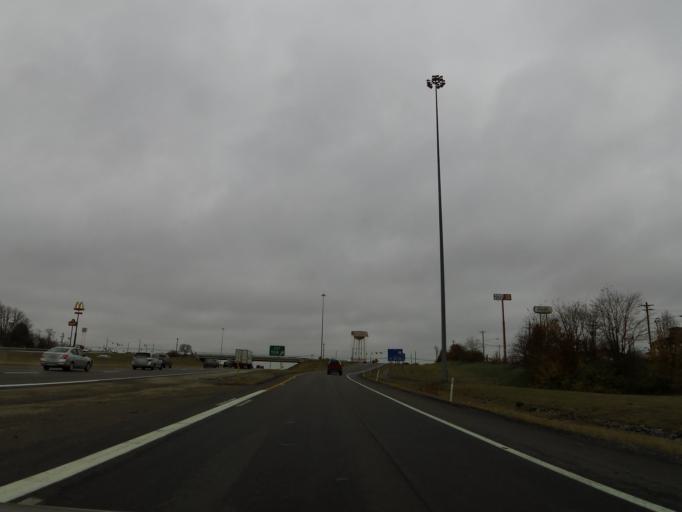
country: US
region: Kentucky
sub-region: Grant County
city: Dry Ridge
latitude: 38.6857
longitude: -84.6020
